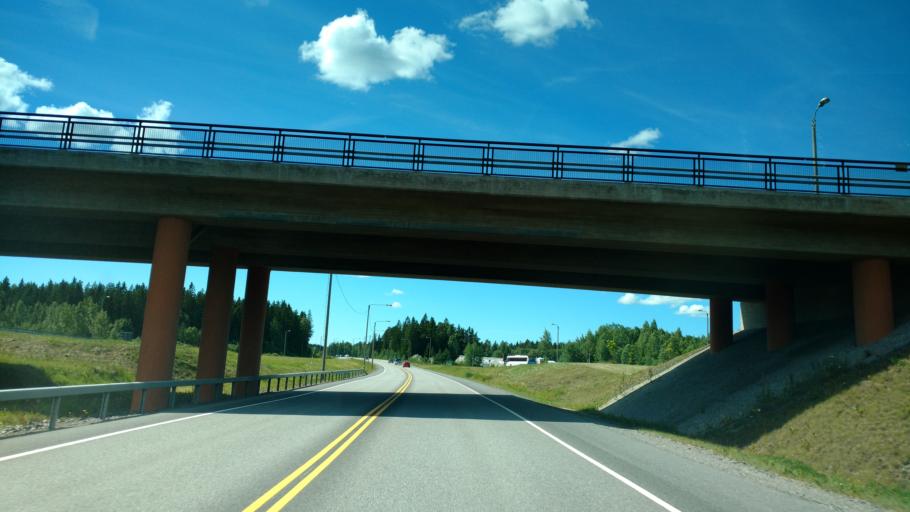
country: FI
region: Varsinais-Suomi
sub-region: Turku
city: Lieto
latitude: 60.4647
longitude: 22.4123
